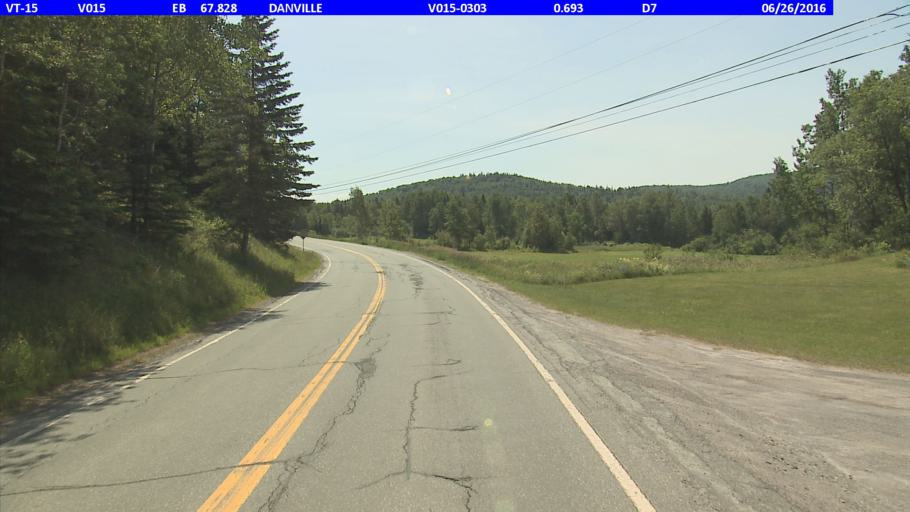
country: US
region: Vermont
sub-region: Caledonia County
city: Hardwick
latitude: 44.4131
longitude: -72.2164
